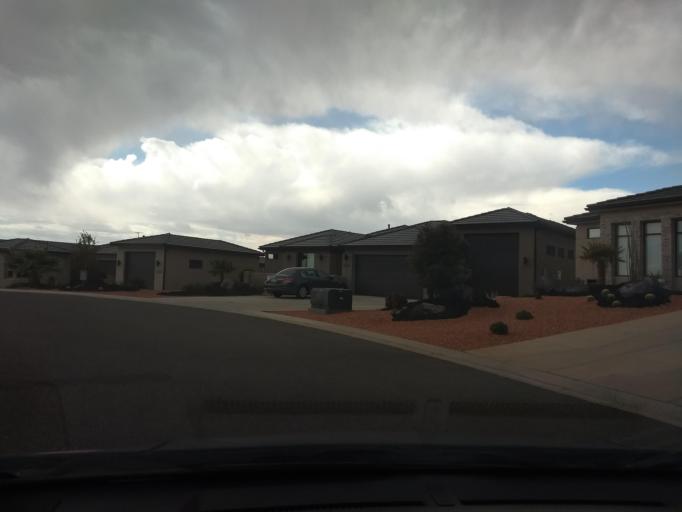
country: US
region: Utah
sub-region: Washington County
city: Washington
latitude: 37.1615
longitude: -113.5250
